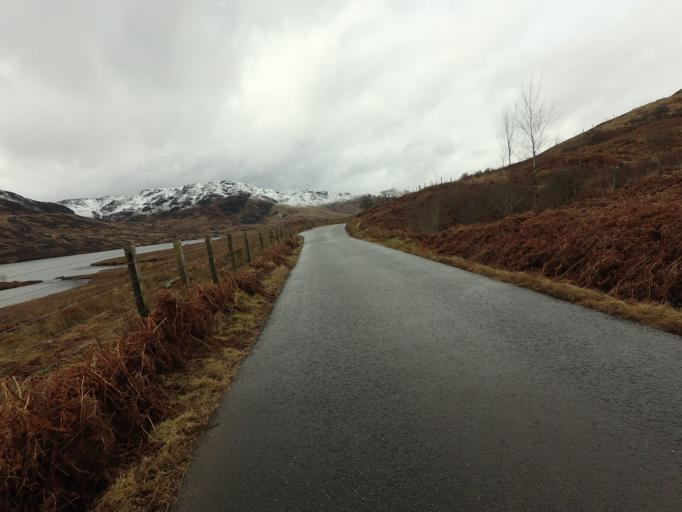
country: GB
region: Scotland
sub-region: West Dunbartonshire
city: Balloch
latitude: 56.2512
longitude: -4.6016
